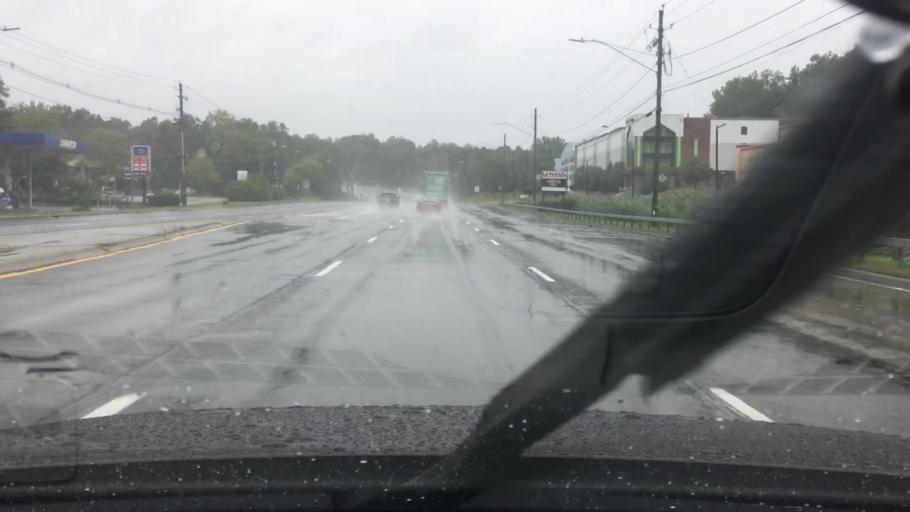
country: US
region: New York
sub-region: Dutchess County
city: Spackenkill
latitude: 41.6400
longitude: -73.9196
